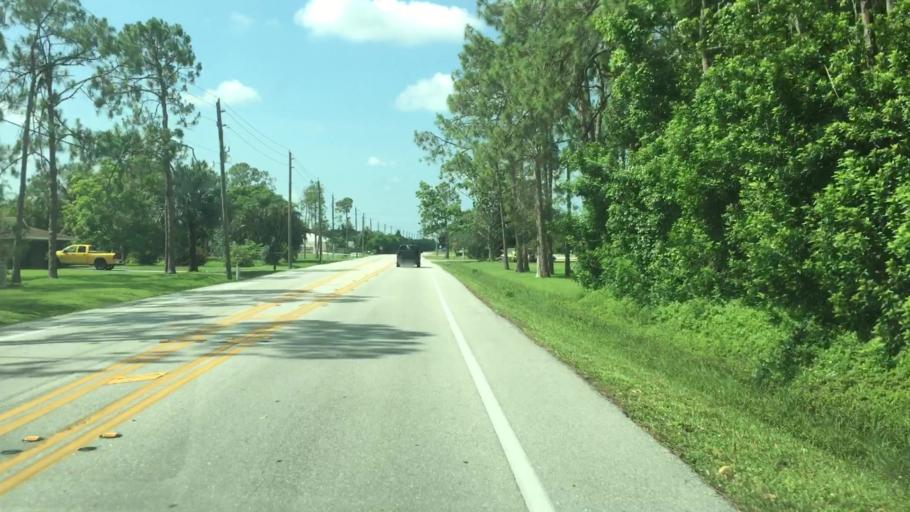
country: US
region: Florida
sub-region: Lee County
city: Villas
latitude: 26.5564
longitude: -81.8467
